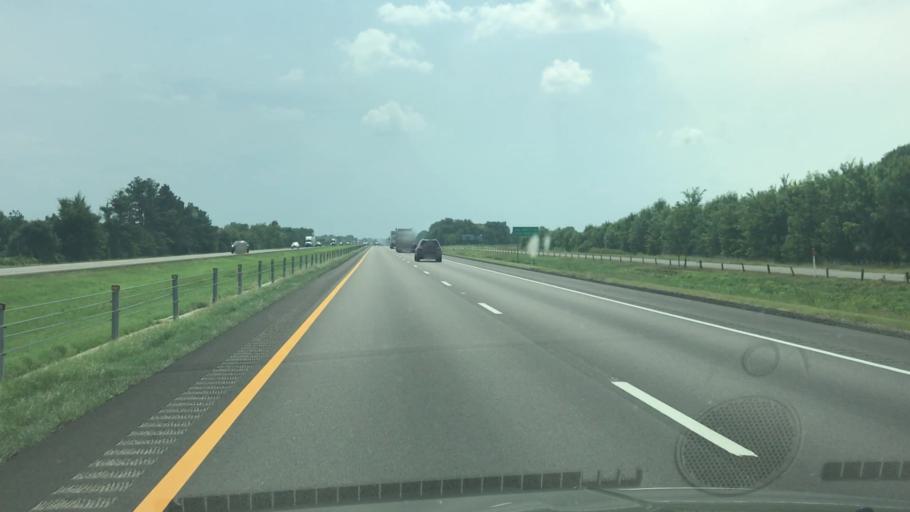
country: US
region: Arkansas
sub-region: Crittenden County
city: Earle
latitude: 35.1458
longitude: -90.4137
